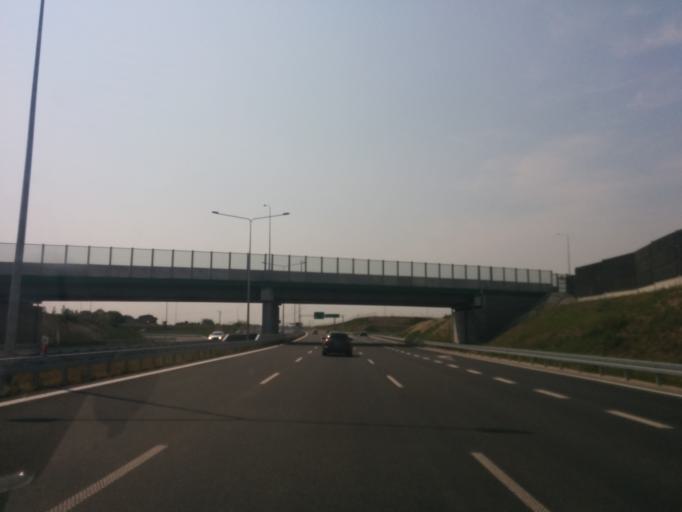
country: PL
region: Masovian Voivodeship
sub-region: Powiat pruszkowski
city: Nowe Grocholice
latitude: 52.1441
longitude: 20.8860
